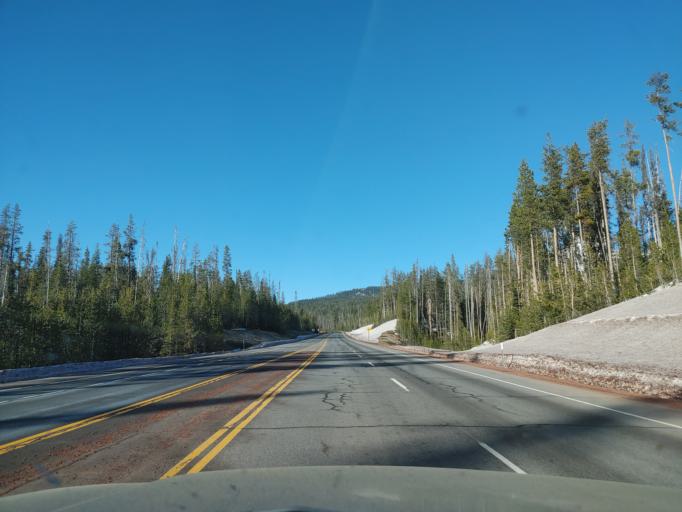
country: US
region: Oregon
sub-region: Lane County
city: Oakridge
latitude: 43.1274
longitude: -122.1316
